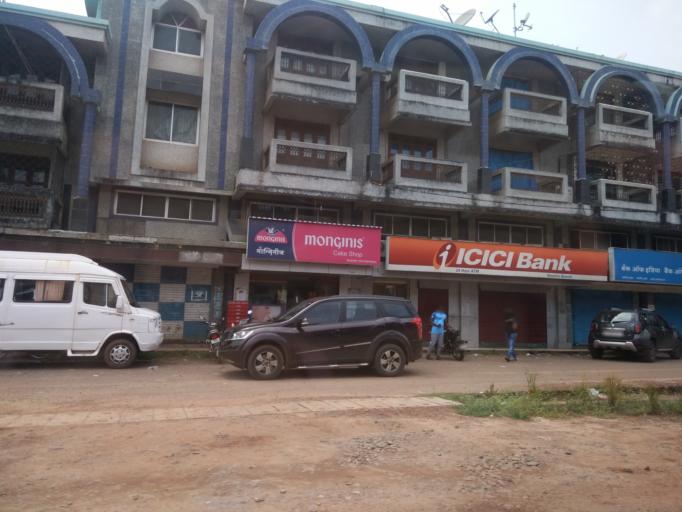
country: IN
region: Goa
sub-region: South Goa
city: Madgaon
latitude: 15.2551
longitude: 73.9674
